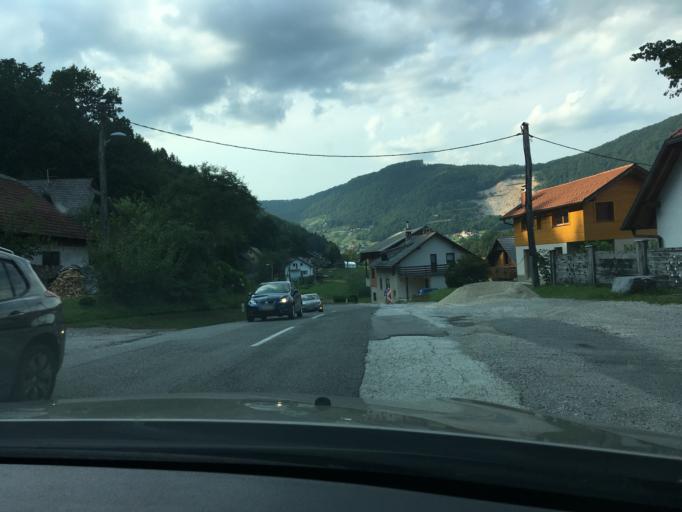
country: SI
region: Dolenjske Toplice
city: Dolenjske Toplice
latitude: 45.7671
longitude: 15.0259
